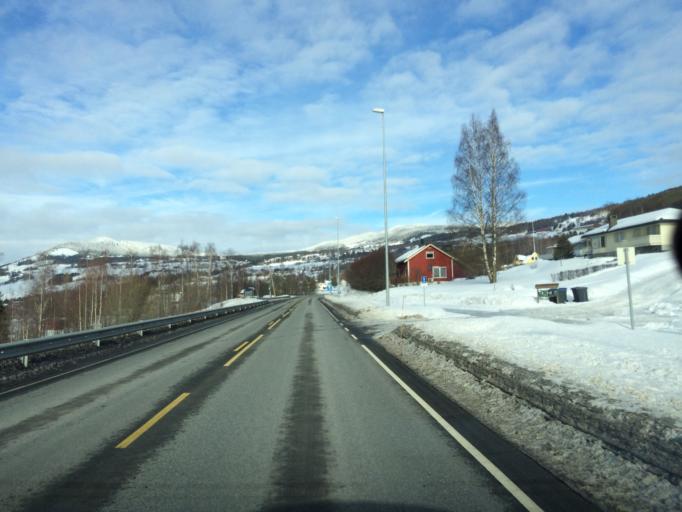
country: NO
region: Oppland
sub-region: Gausdal
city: Segalstad bru
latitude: 61.2064
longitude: 10.2997
